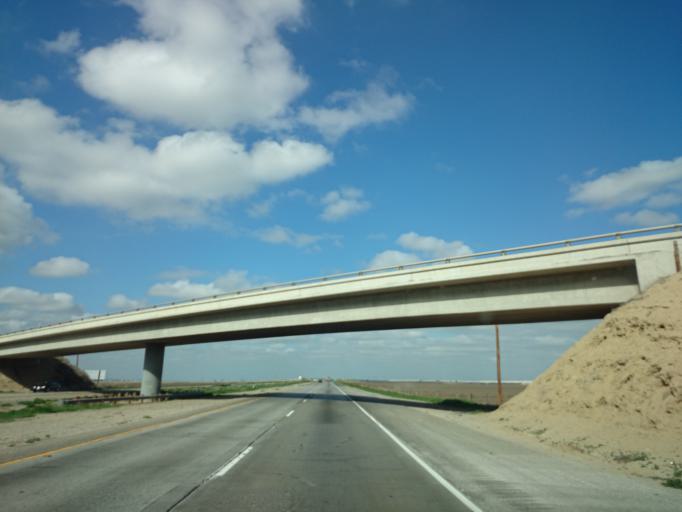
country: US
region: California
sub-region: Kern County
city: Greenfield
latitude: 35.1515
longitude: -119.0993
